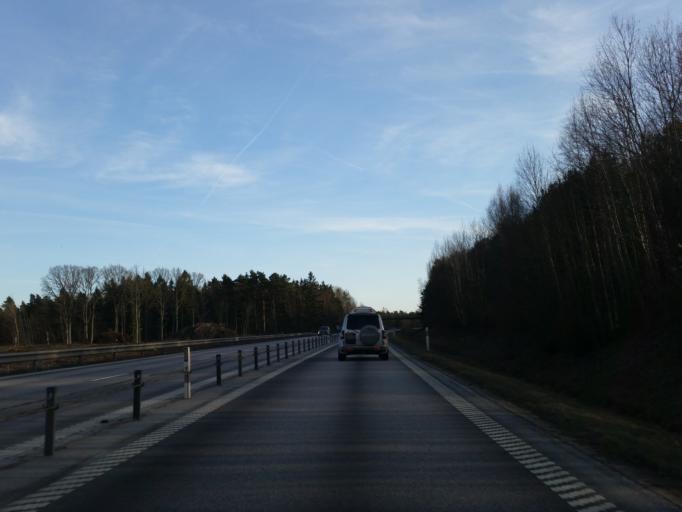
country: SE
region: Kalmar
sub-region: Kalmar Kommun
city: Lindsdal
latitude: 56.7295
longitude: 16.3136
